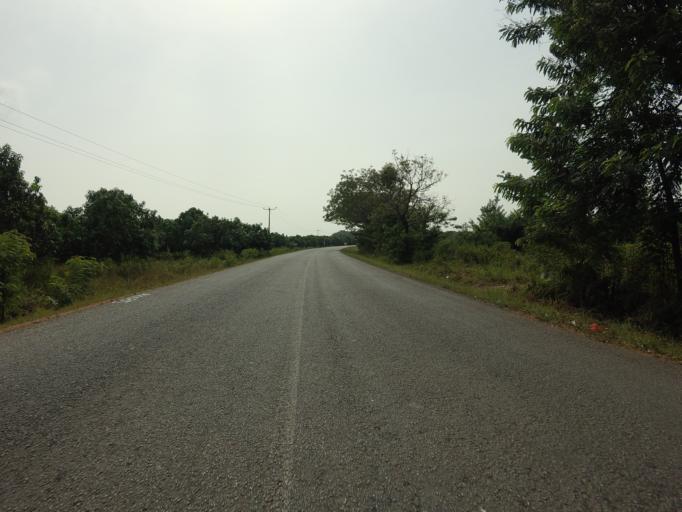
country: GH
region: Volta
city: Ho
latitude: 6.4035
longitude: 0.1772
